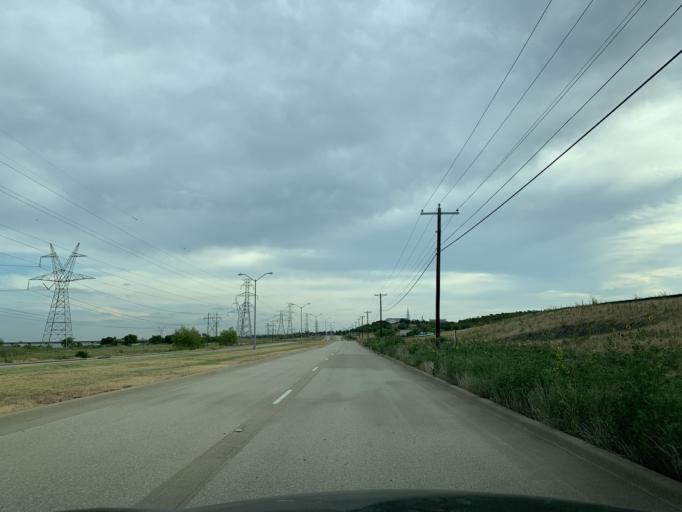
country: US
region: Texas
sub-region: Dallas County
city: Grand Prairie
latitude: 32.6997
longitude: -96.9599
